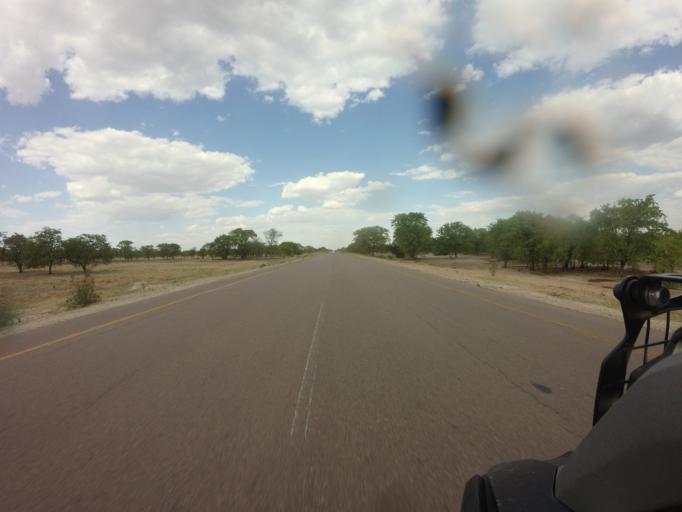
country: AO
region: Cunene
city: Ondjiva
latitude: -16.7517
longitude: 15.0676
